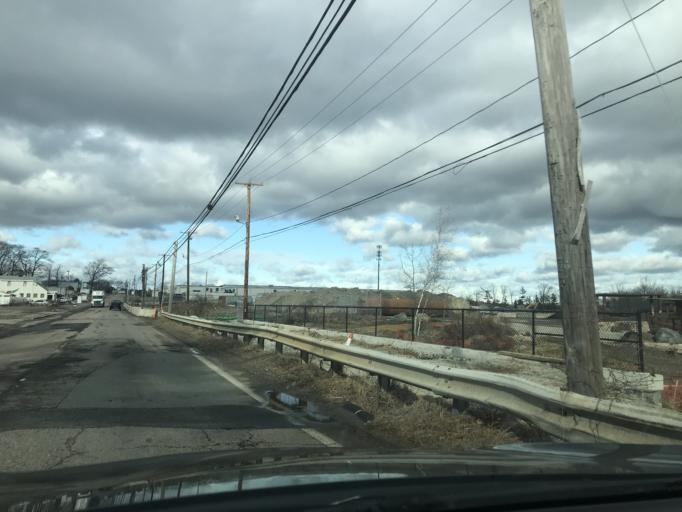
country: US
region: Massachusetts
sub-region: Plymouth County
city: Abington
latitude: 42.1395
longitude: -70.9513
